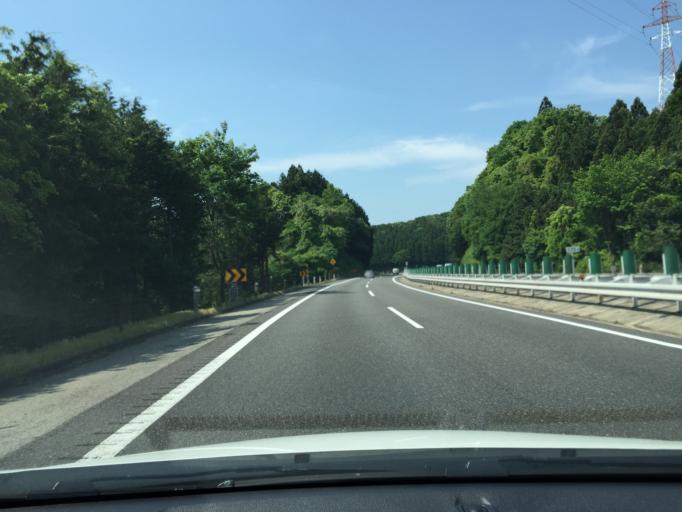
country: JP
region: Fukushima
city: Sukagawa
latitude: 37.1476
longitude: 140.2406
